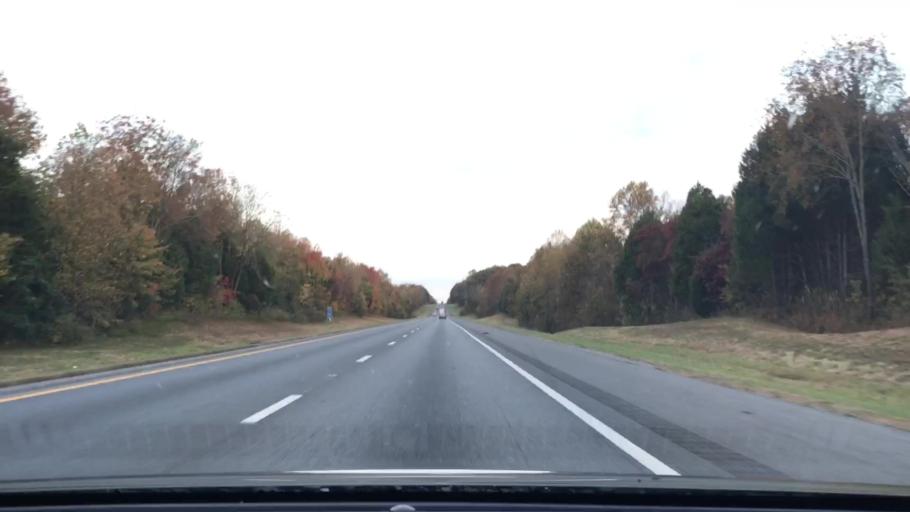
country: US
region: Tennessee
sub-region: Cheatham County
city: Pleasant View
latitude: 36.4797
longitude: -87.1464
